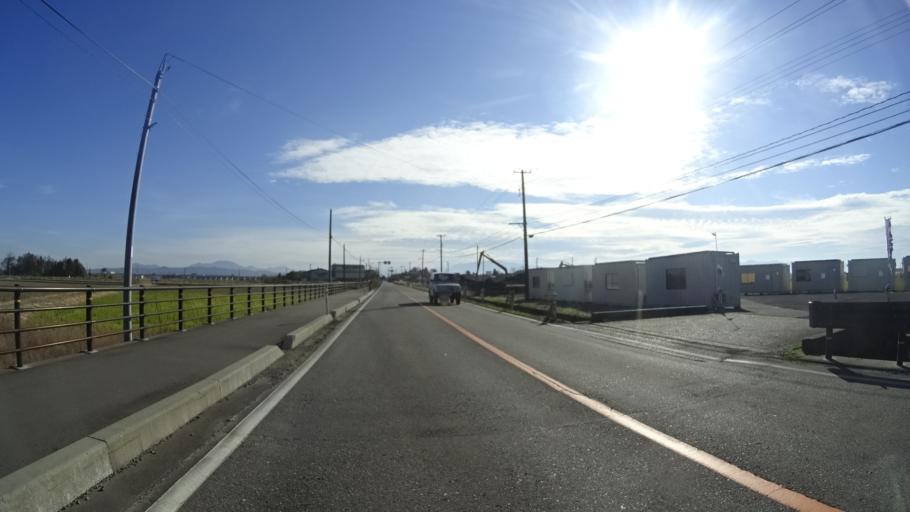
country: JP
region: Niigata
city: Mitsuke
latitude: 37.5528
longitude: 138.8625
